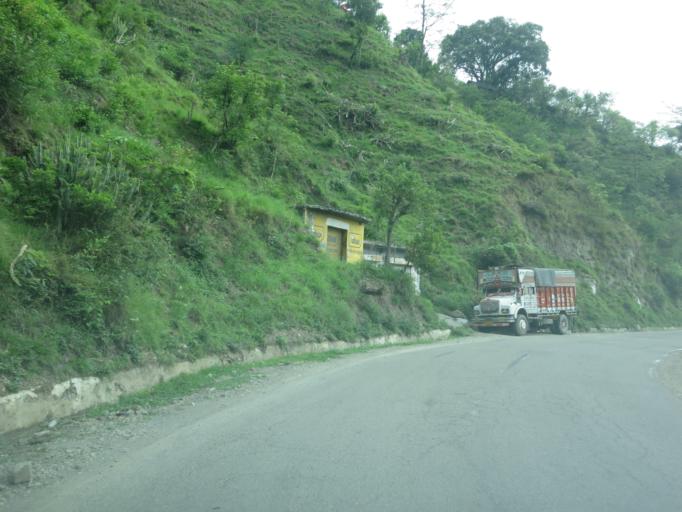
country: IN
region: Himachal Pradesh
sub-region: Solan
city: Arki
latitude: 31.2534
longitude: 76.8733
